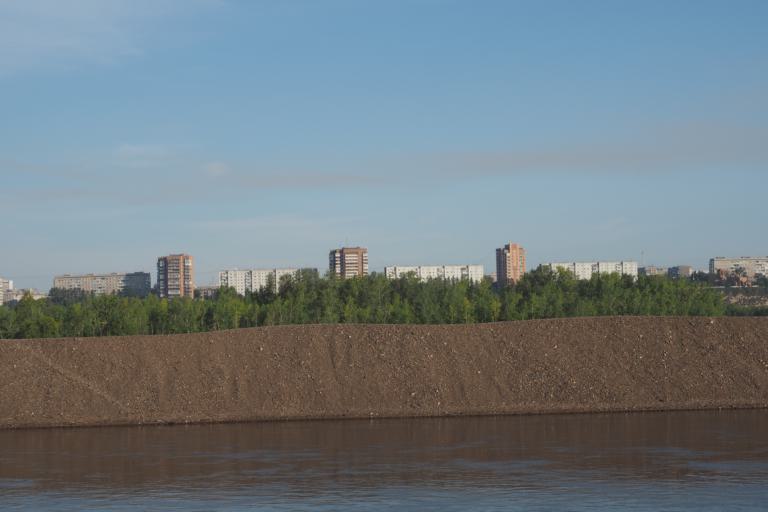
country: RU
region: Krasnoyarskiy
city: Solnechnyy
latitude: 56.0370
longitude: 92.9929
